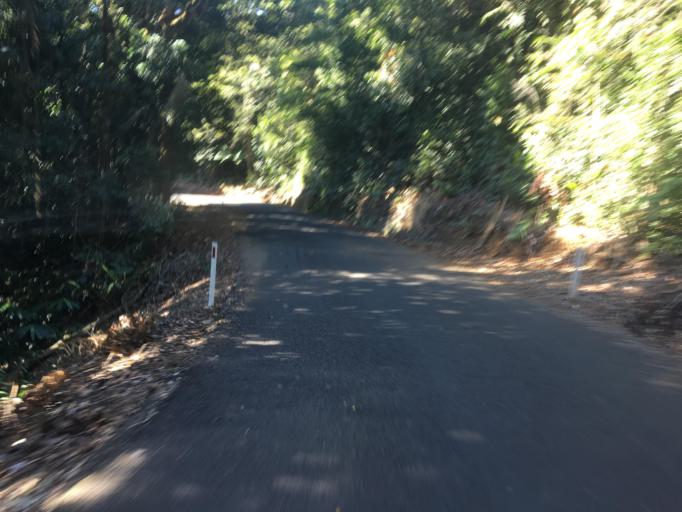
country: AU
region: Queensland
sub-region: Tablelands
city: Ravenshoe
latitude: -17.5894
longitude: 145.5917
